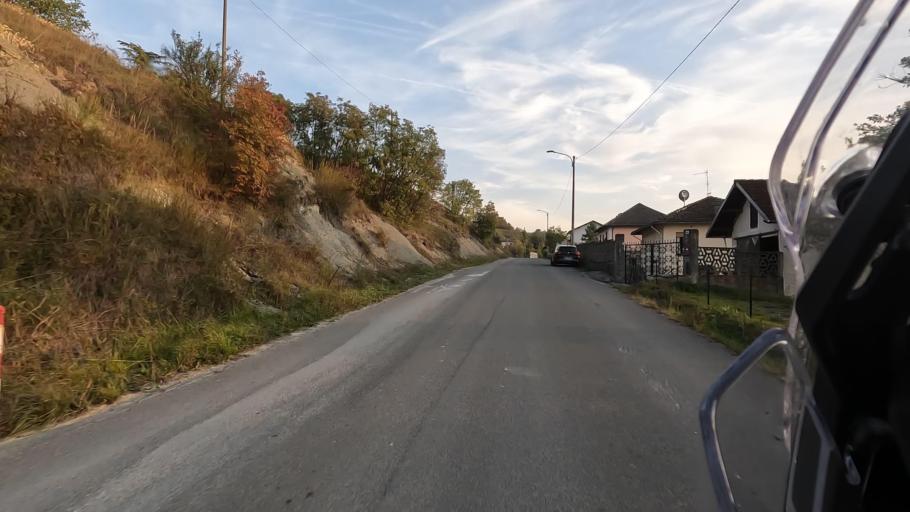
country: IT
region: Liguria
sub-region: Provincia di Savona
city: Mioglia
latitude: 44.4812
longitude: 8.4135
